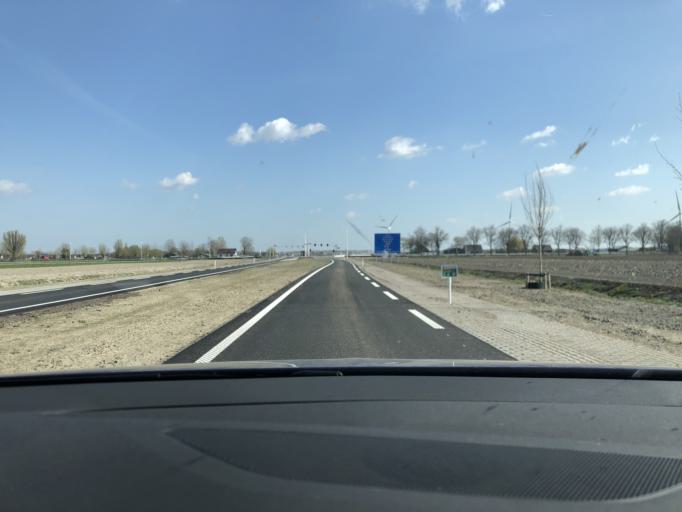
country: NL
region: South Holland
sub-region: Gemeente Waddinxveen
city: Groenswaard
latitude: 52.0307
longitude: 4.6270
